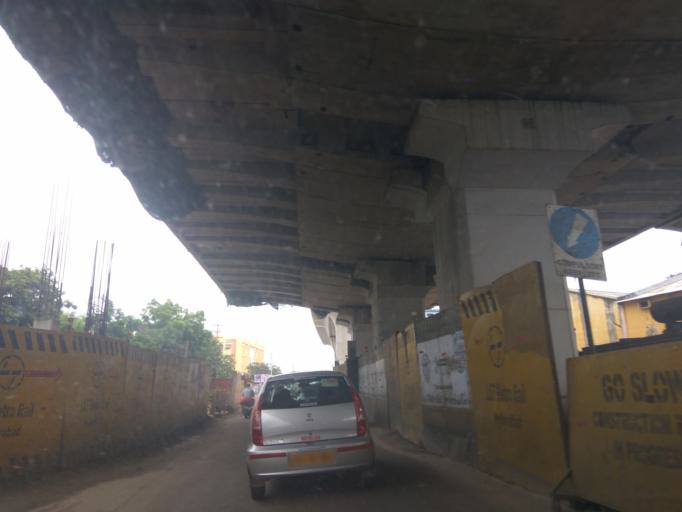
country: IN
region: Telangana
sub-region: Hyderabad
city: Malkajgiri
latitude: 17.4253
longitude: 78.5019
